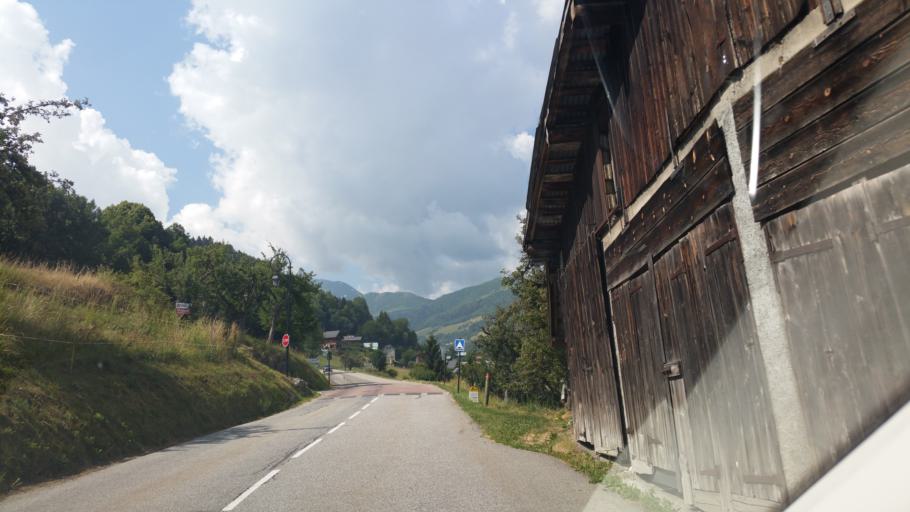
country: FR
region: Rhone-Alpes
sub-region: Departement de la Savoie
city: Aigueblanche
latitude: 45.4900
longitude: 6.4696
